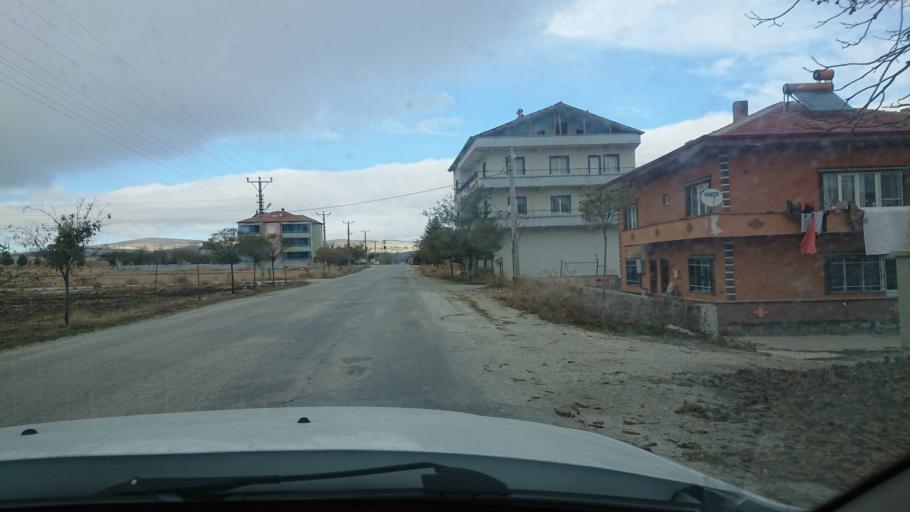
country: TR
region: Aksaray
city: Ortakoy
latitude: 38.7446
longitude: 34.0309
